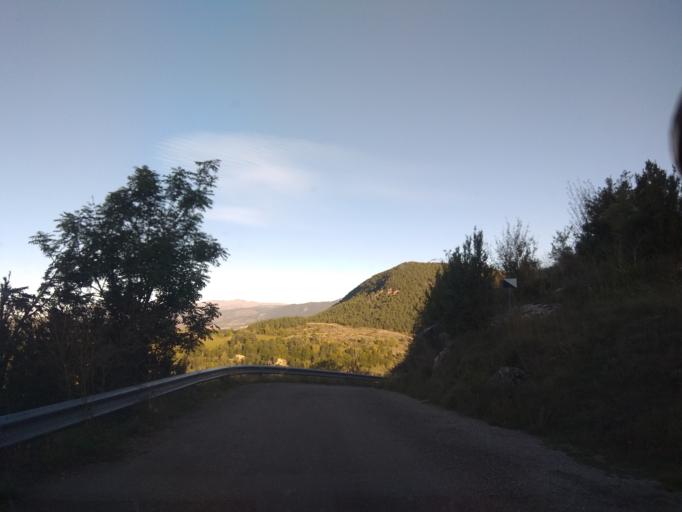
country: ES
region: Catalonia
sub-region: Provincia de Lleida
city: Lles de Cerdanya
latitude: 42.3534
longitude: 1.7181
